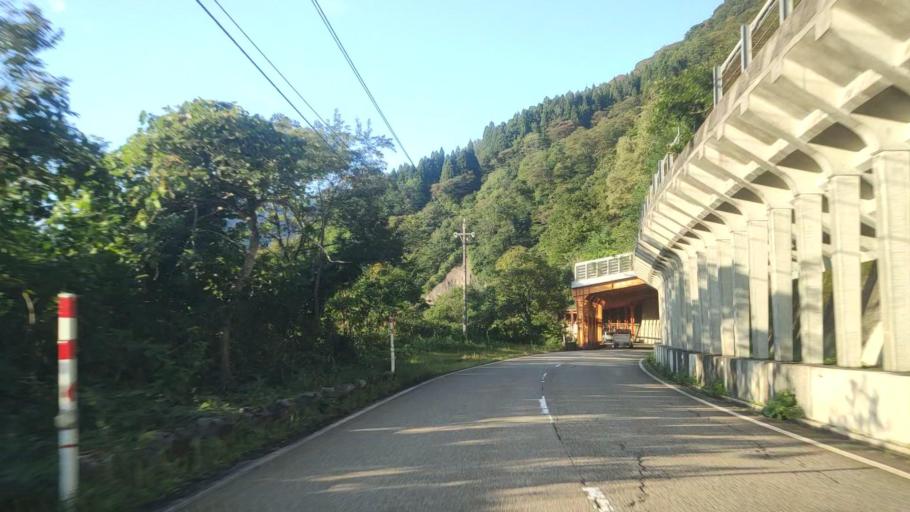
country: JP
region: Toyama
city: Yatsuomachi-higashikumisaka
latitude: 36.5210
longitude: 137.0282
